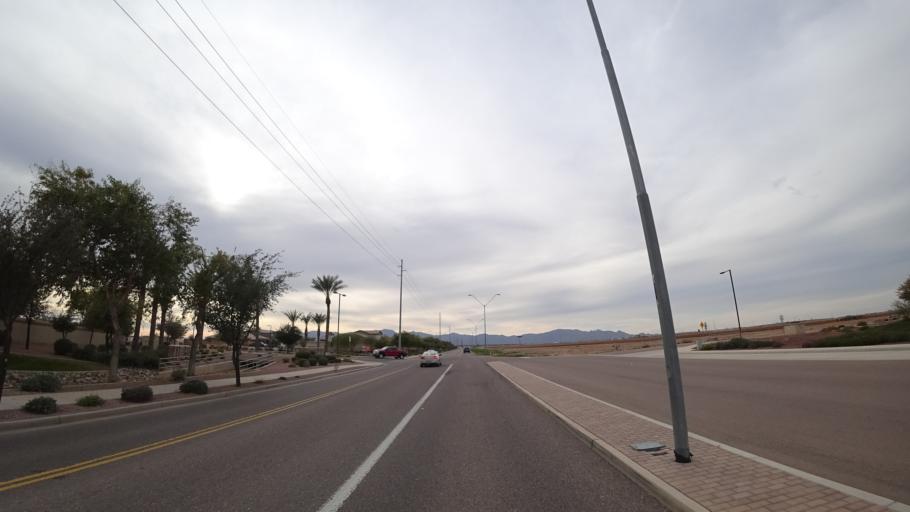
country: US
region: Arizona
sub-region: Maricopa County
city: Citrus Park
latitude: 33.5951
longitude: -112.4018
